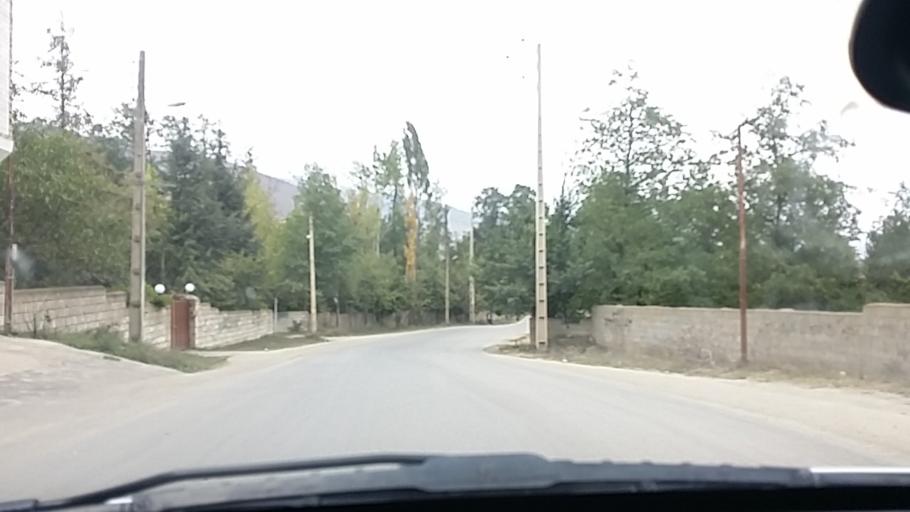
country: IR
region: Mazandaran
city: `Abbasabad
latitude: 36.5022
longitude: 51.1639
